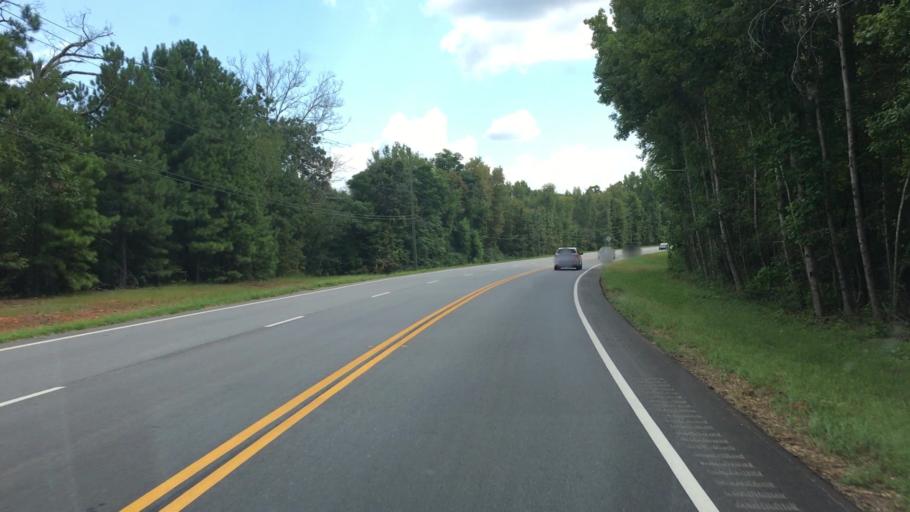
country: US
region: Georgia
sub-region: Putnam County
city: Jefferson
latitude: 33.4269
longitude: -83.3706
